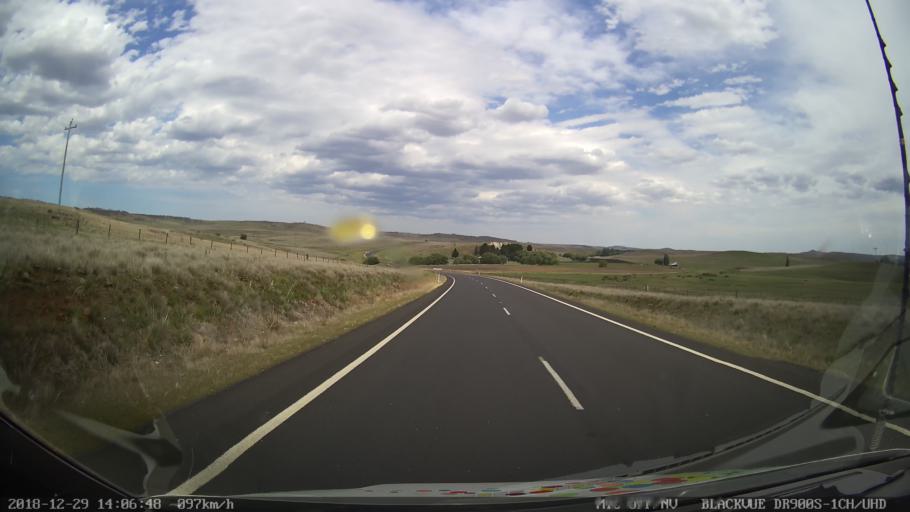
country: AU
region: New South Wales
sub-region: Cooma-Monaro
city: Cooma
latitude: -36.3441
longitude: 149.2075
